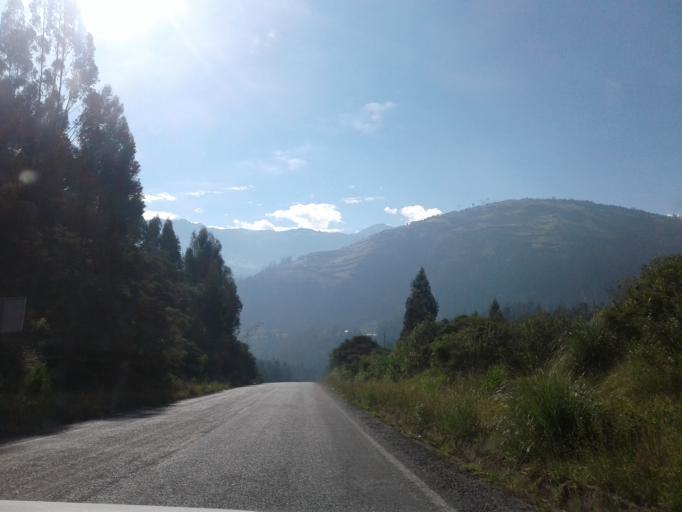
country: EC
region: Chimborazo
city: Guano
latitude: -1.5183
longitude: -78.5114
